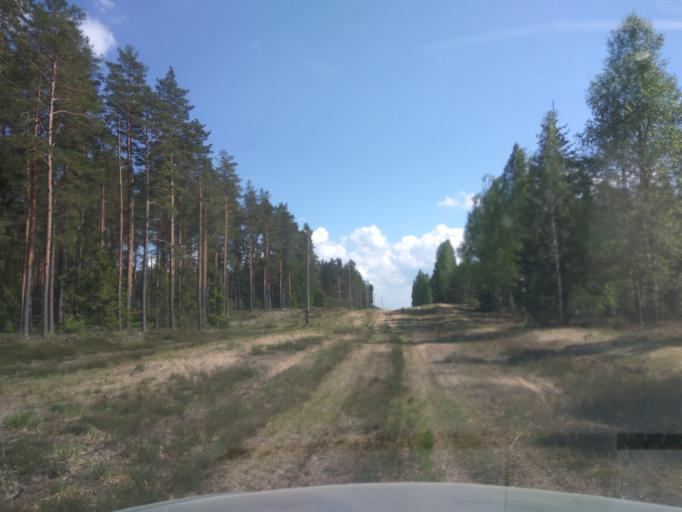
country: LV
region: Kuldigas Rajons
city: Kuldiga
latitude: 57.1833
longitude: 21.9974
